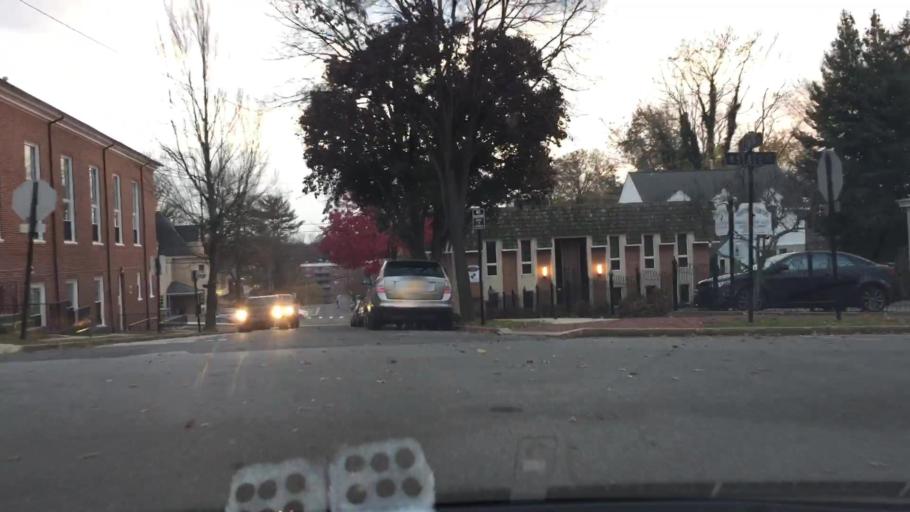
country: US
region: Pennsylvania
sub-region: Delaware County
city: Media
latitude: 39.9196
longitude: -75.3947
